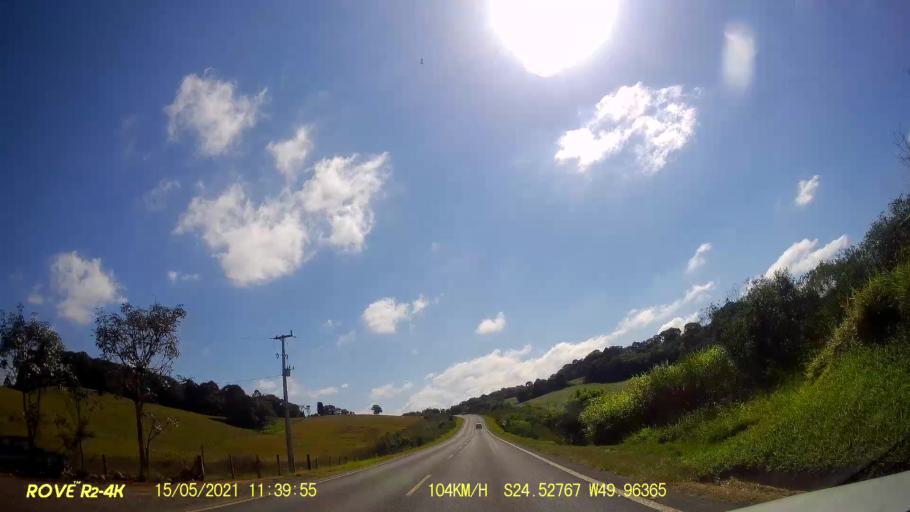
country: BR
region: Parana
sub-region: Pirai Do Sul
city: Pirai do Sul
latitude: -24.5283
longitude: -49.9634
